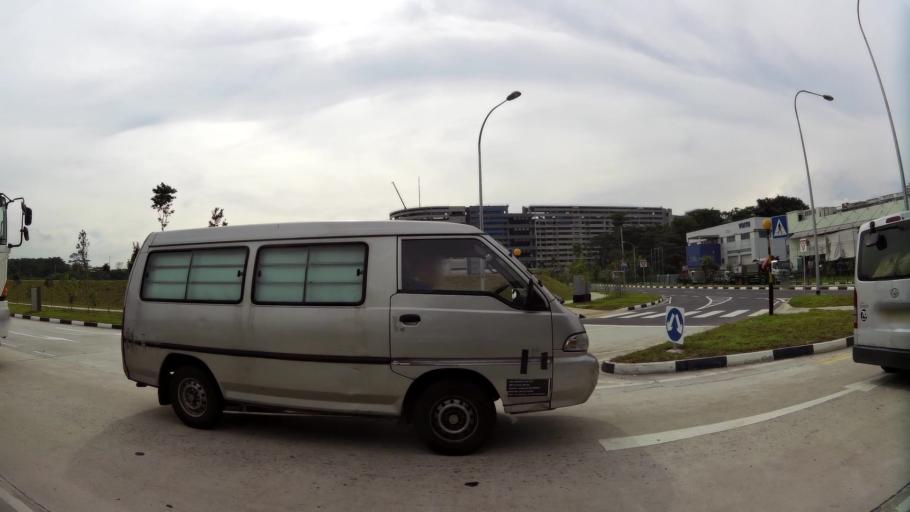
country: MY
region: Johor
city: Johor Bahru
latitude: 1.4313
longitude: 103.7557
